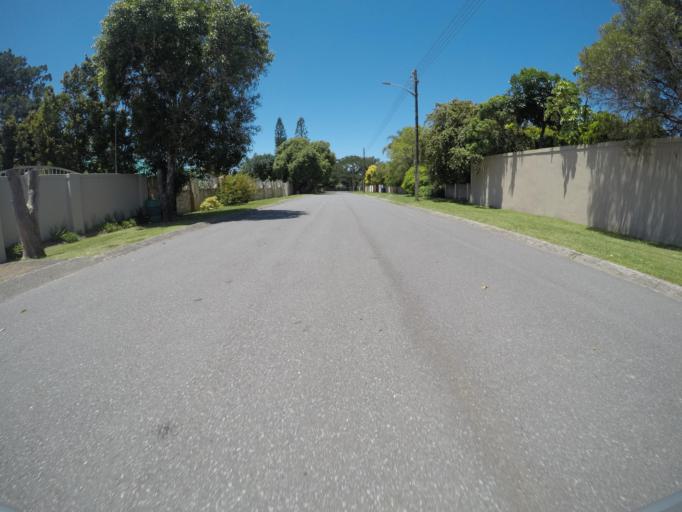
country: ZA
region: Eastern Cape
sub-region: Buffalo City Metropolitan Municipality
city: East London
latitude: -32.9656
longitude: 27.9447
